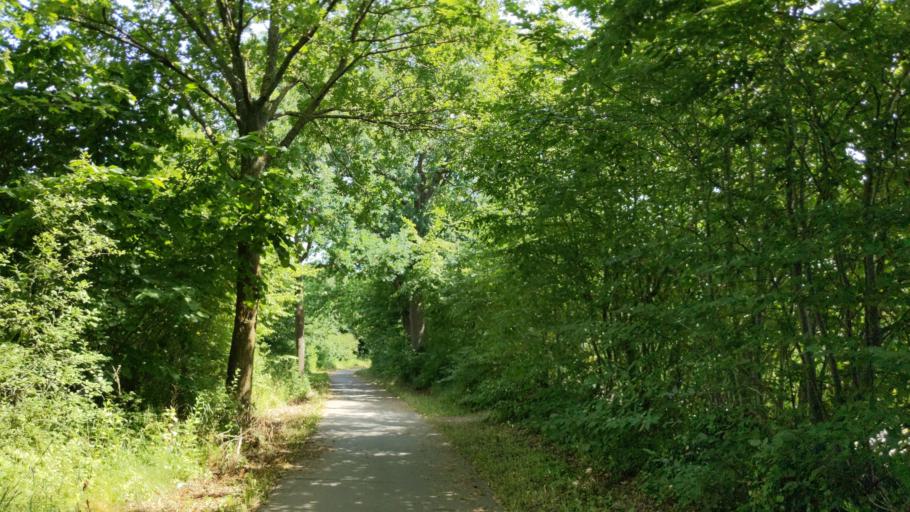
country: DE
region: Schleswig-Holstein
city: Bosdorf
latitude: 54.1483
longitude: 10.5238
